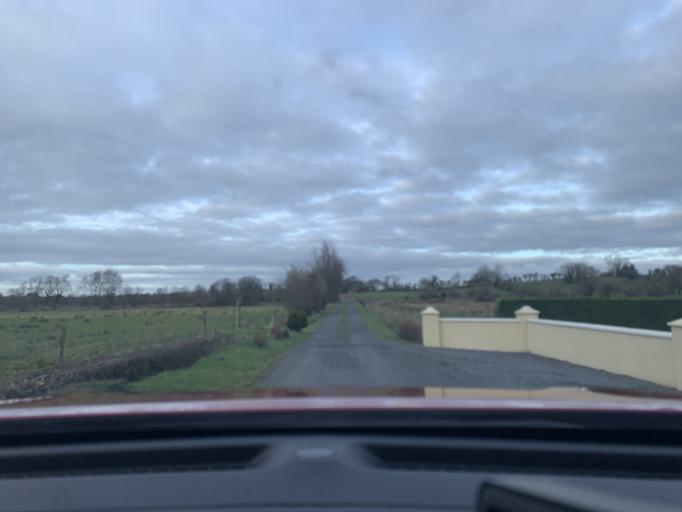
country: IE
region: Connaught
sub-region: Sligo
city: Ballymote
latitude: 54.0107
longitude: -8.5730
